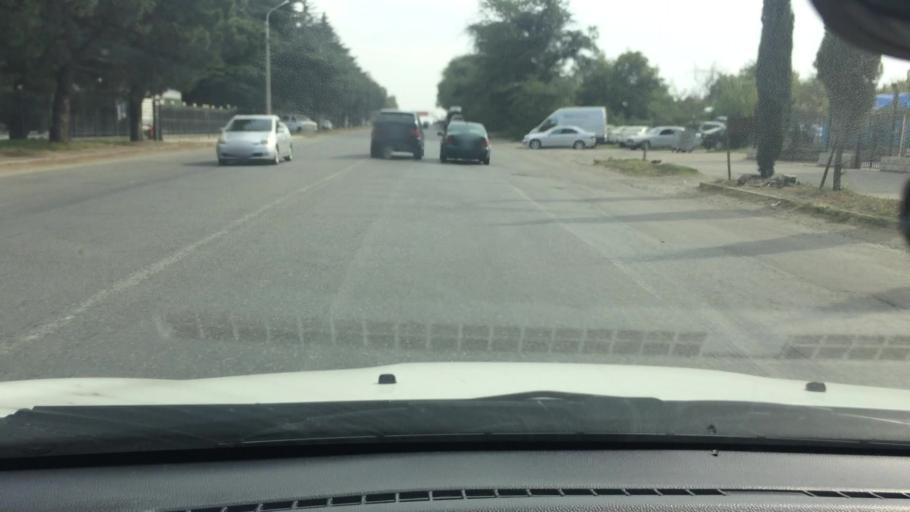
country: GE
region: T'bilisi
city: Tbilisi
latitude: 41.6434
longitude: 44.9125
